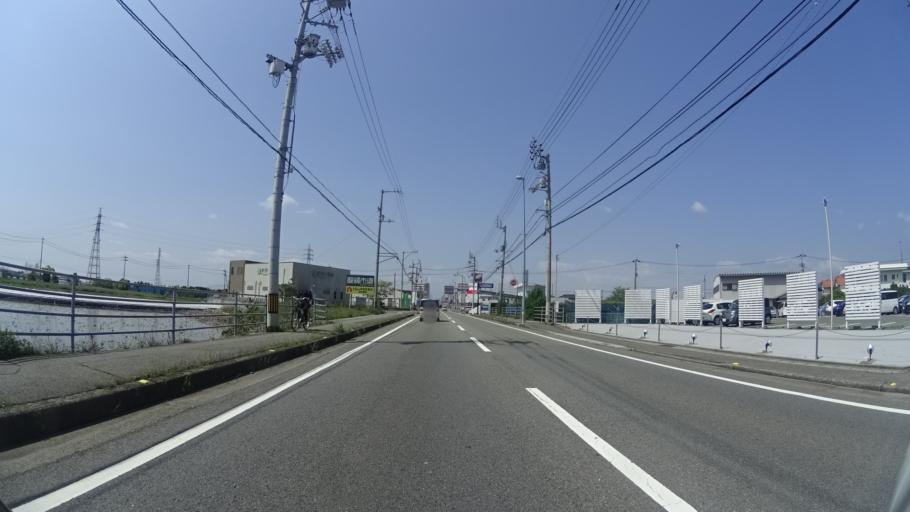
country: JP
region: Tokushima
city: Narutocho-mitsuishi
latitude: 34.1657
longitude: 134.5982
